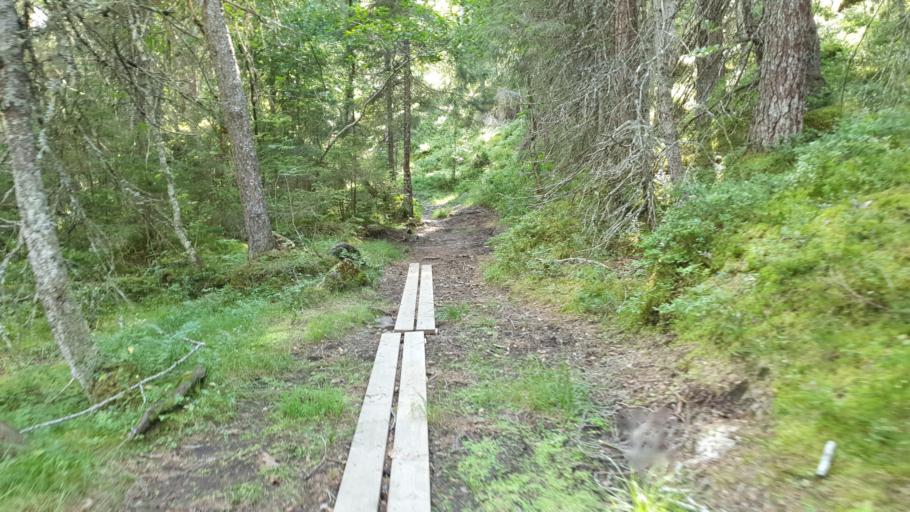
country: NO
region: Nord-Trondelag
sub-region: Levanger
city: Levanger
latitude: 63.6914
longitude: 11.2715
